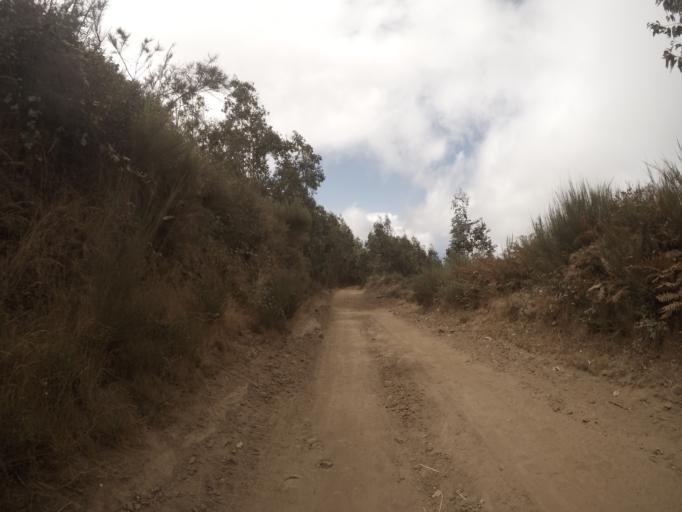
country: PT
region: Madeira
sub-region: Camara de Lobos
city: Curral das Freiras
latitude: 32.7104
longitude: -17.0084
